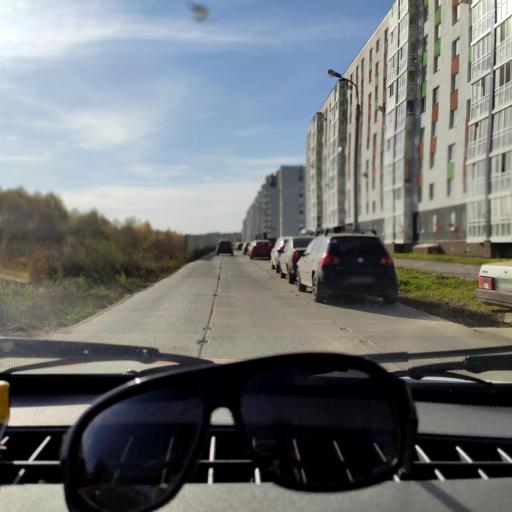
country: RU
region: Bashkortostan
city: Ufa
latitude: 54.6946
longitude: 55.9739
